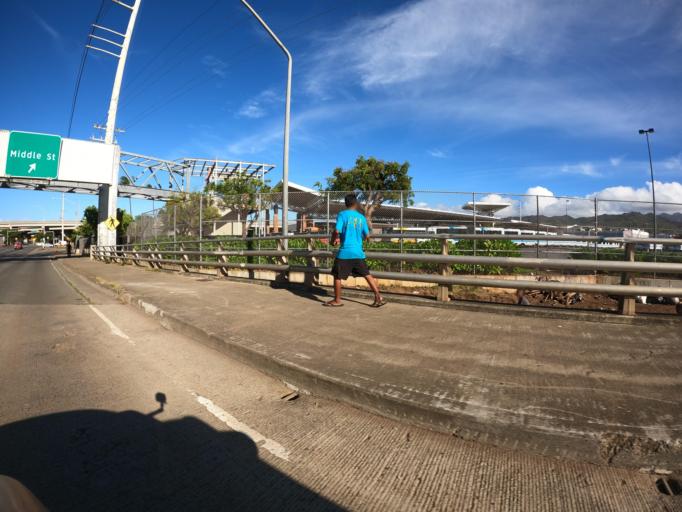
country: US
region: Hawaii
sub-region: Honolulu County
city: Honolulu
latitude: 21.3332
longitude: -157.8884
